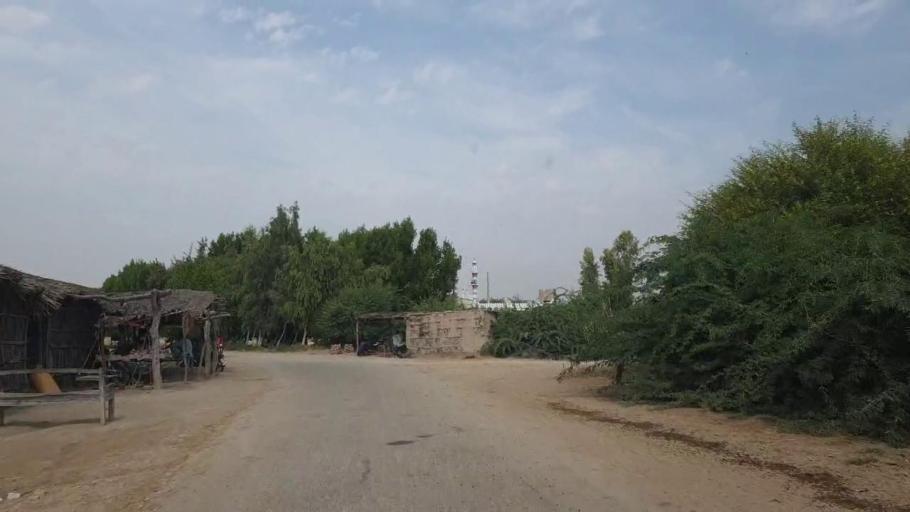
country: PK
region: Sindh
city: Rajo Khanani
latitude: 24.9370
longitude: 68.9863
